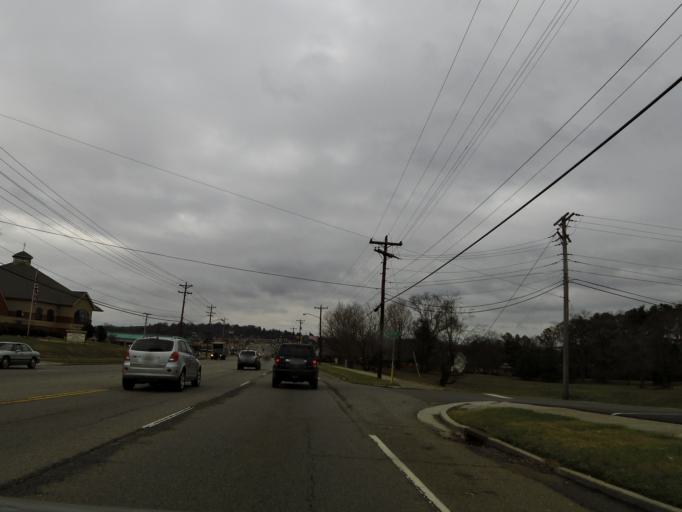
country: US
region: Tennessee
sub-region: Hamblen County
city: Morristown
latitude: 36.2029
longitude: -83.3295
